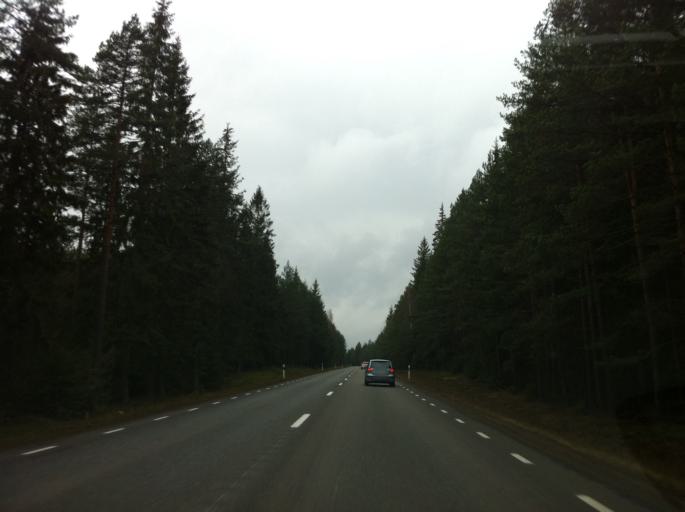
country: SE
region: Joenkoeping
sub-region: Vetlanda Kommun
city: Landsbro
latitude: 57.4078
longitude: 14.9760
